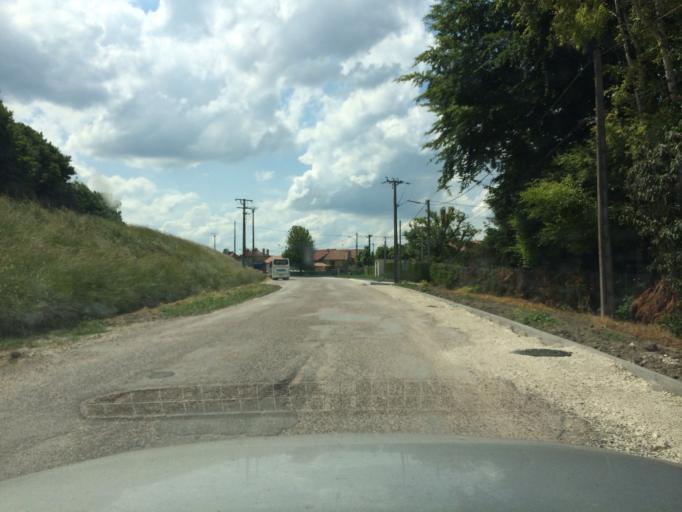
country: FR
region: Lorraine
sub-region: Departement de la Meuse
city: Vacon
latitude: 48.6878
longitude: 5.6262
